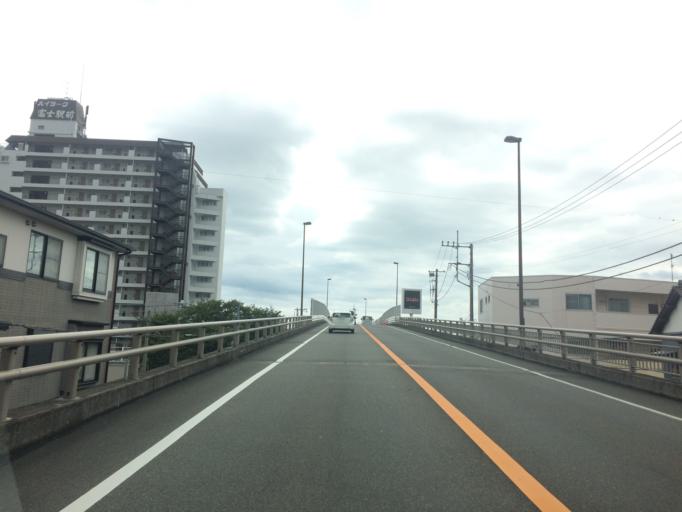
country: JP
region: Shizuoka
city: Fuji
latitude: 35.1523
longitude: 138.6473
